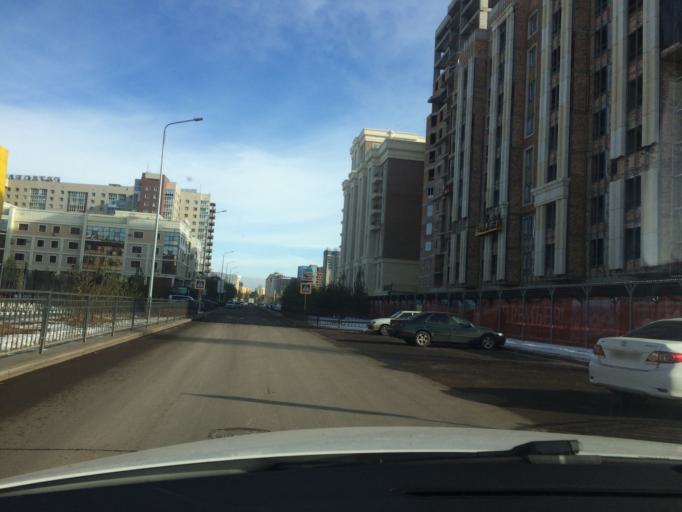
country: KZ
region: Astana Qalasy
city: Astana
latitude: 51.1420
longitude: 71.4154
